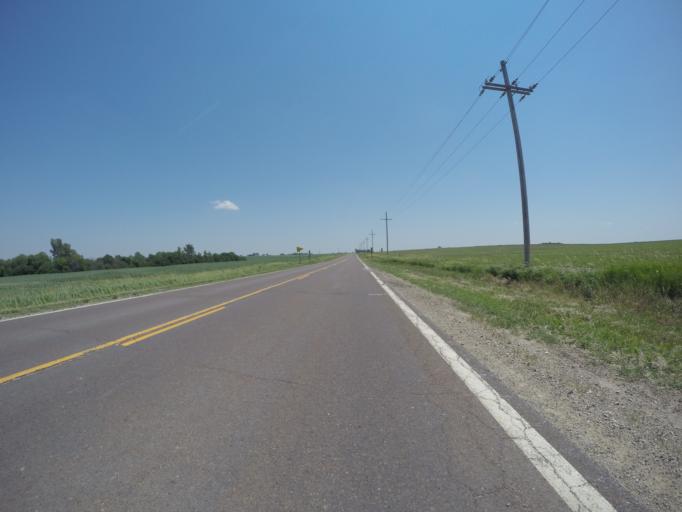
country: US
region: Kansas
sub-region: Doniphan County
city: Troy
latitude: 39.7403
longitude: -95.2135
